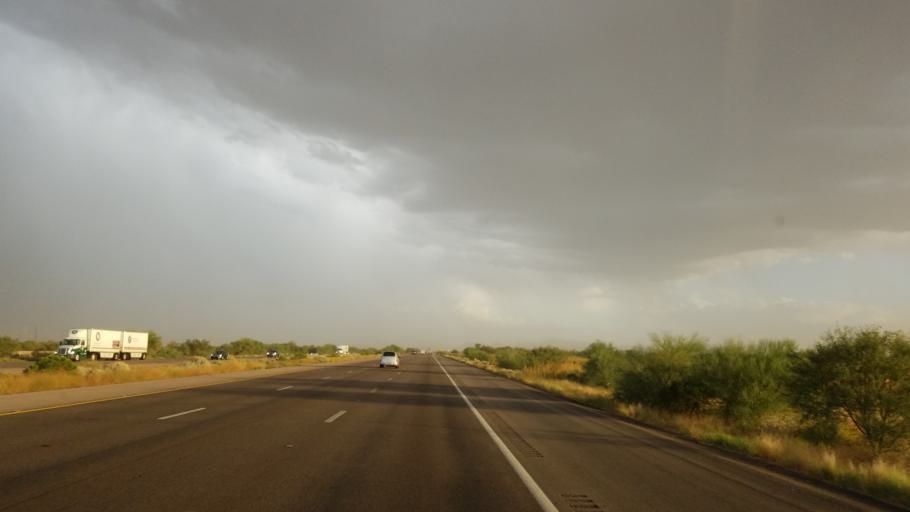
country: US
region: Arizona
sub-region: Pima County
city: Avra Valley
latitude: 32.5457
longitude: -111.3002
